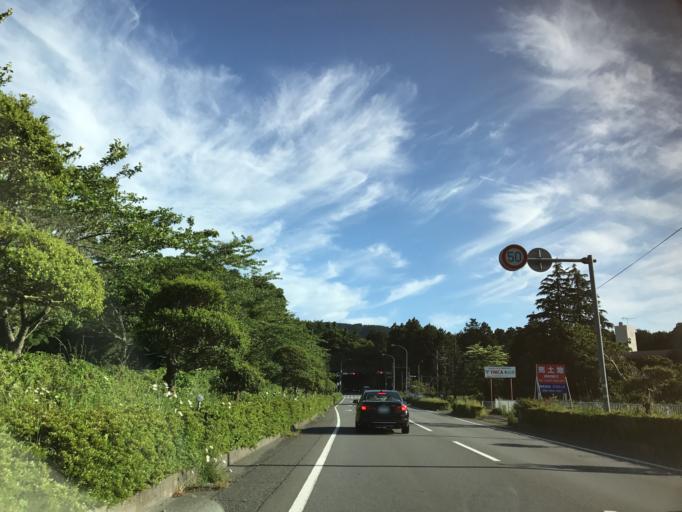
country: JP
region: Shizuoka
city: Gotemba
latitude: 35.2911
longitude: 138.9561
